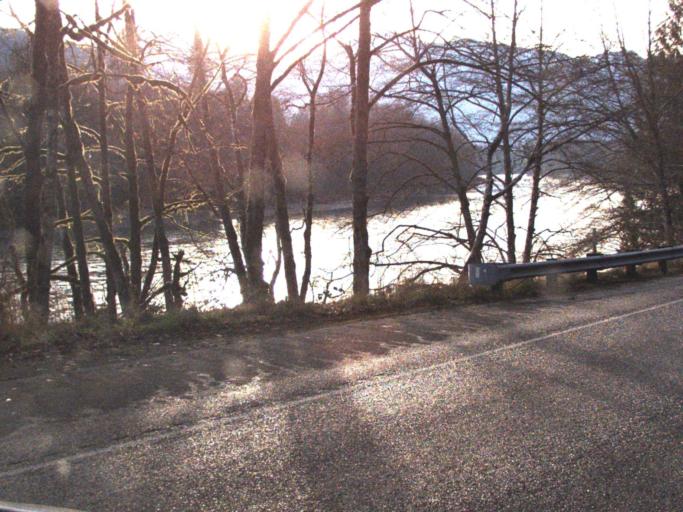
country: US
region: Washington
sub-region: Snohomish County
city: Darrington
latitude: 48.5434
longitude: -121.7960
